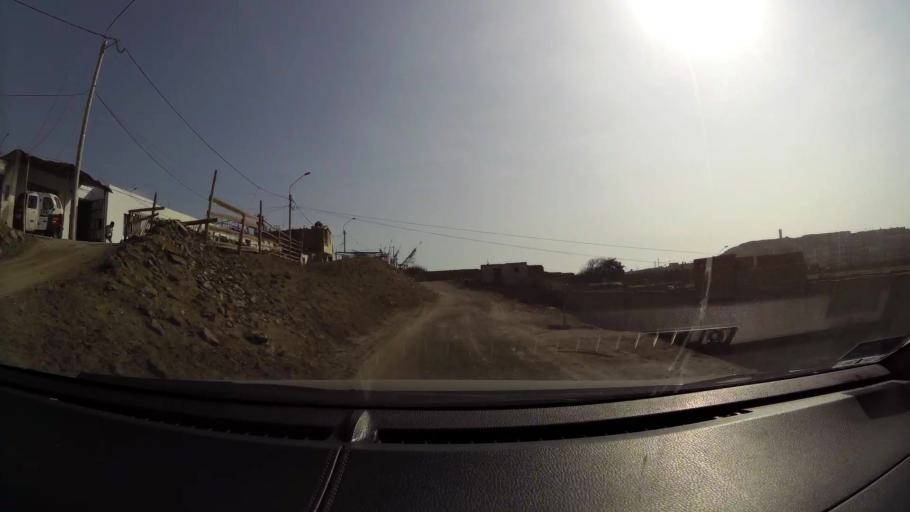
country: PE
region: Lima
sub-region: Huaura
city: Huacho
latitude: -11.1283
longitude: -77.6146
